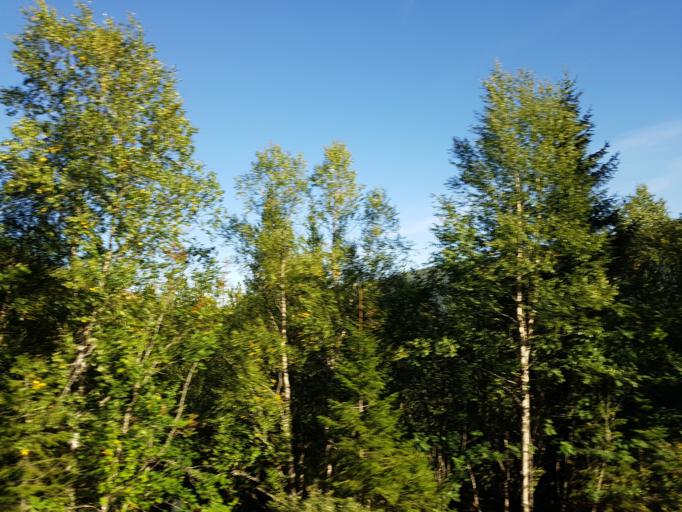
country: NO
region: Sor-Trondelag
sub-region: Afjord
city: A i Afjord
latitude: 63.6915
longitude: 10.2448
